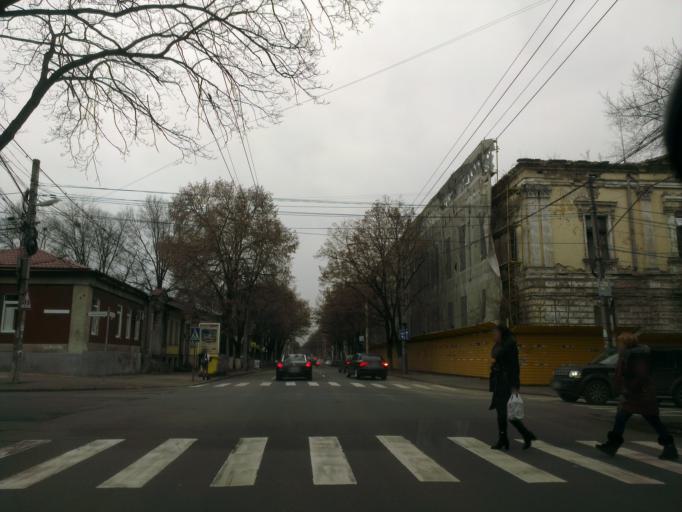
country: MD
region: Chisinau
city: Chisinau
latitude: 47.0196
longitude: 28.8312
